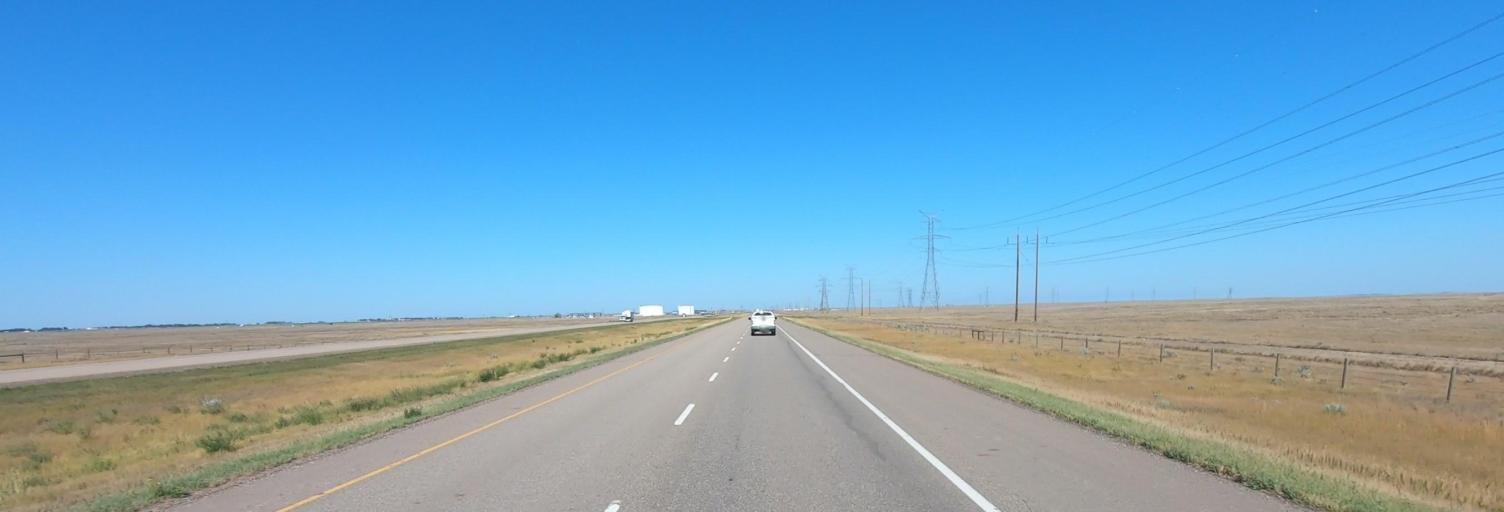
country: CA
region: Alberta
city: Brooks
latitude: 50.4478
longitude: -111.5694
